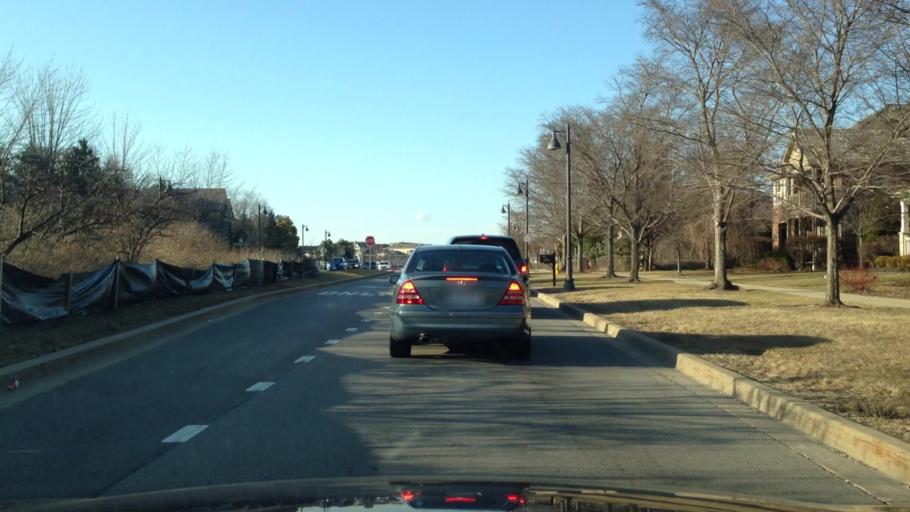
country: US
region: Illinois
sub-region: Cook County
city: Glenview
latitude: 42.0812
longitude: -87.8194
